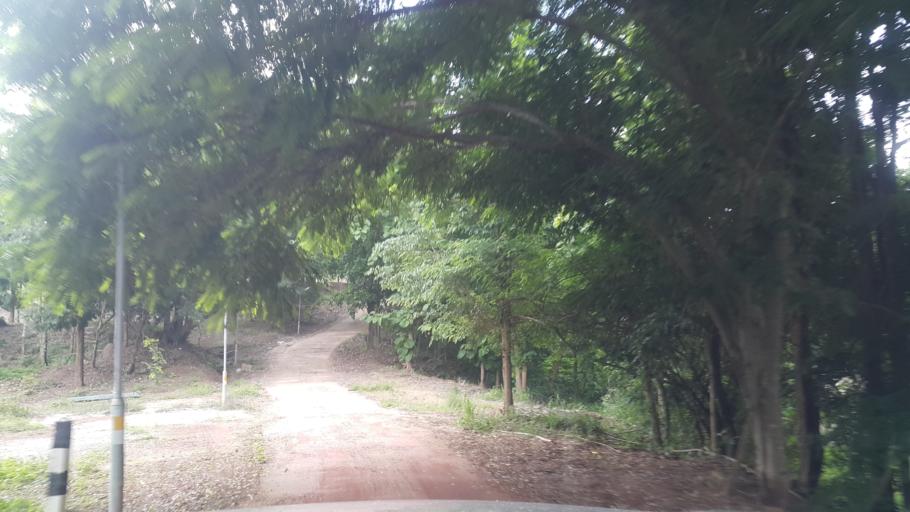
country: TH
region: Chiang Mai
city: Mae Taeng
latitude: 19.2252
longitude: 99.0102
